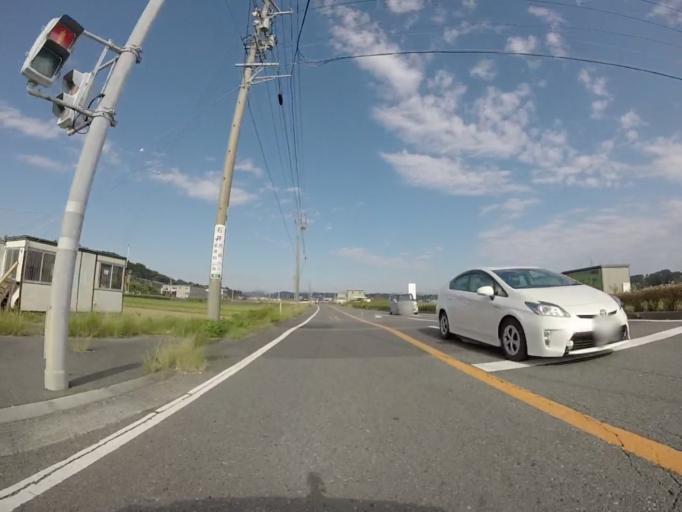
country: JP
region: Shizuoka
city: Shimada
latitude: 34.7639
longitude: 138.2391
